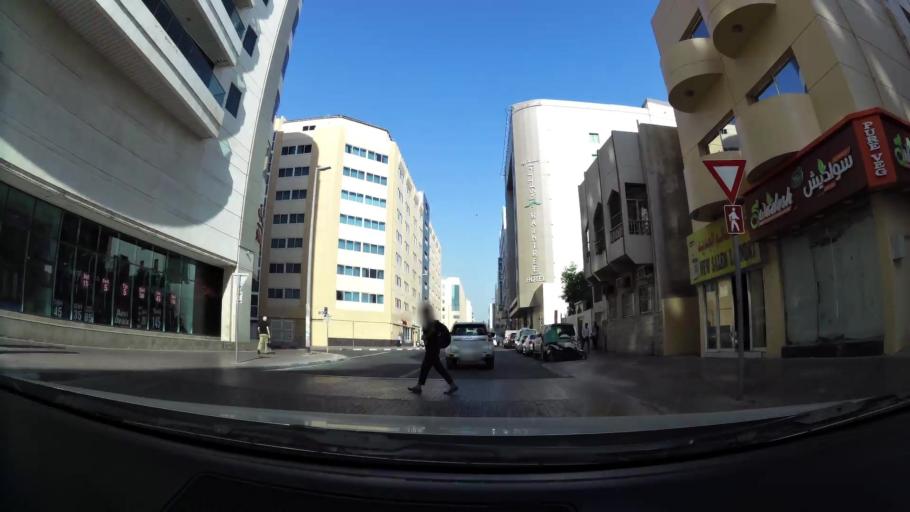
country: AE
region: Ash Shariqah
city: Sharjah
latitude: 25.2568
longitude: 55.2940
